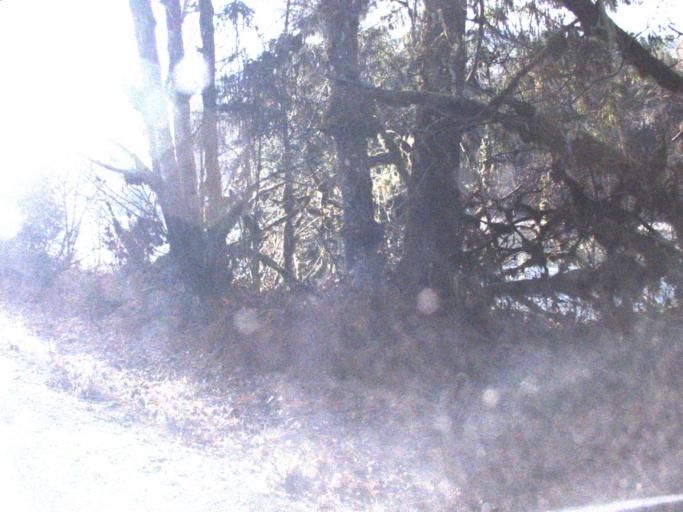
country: US
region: Washington
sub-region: Snohomish County
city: Darrington
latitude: 48.3961
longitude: -121.5505
